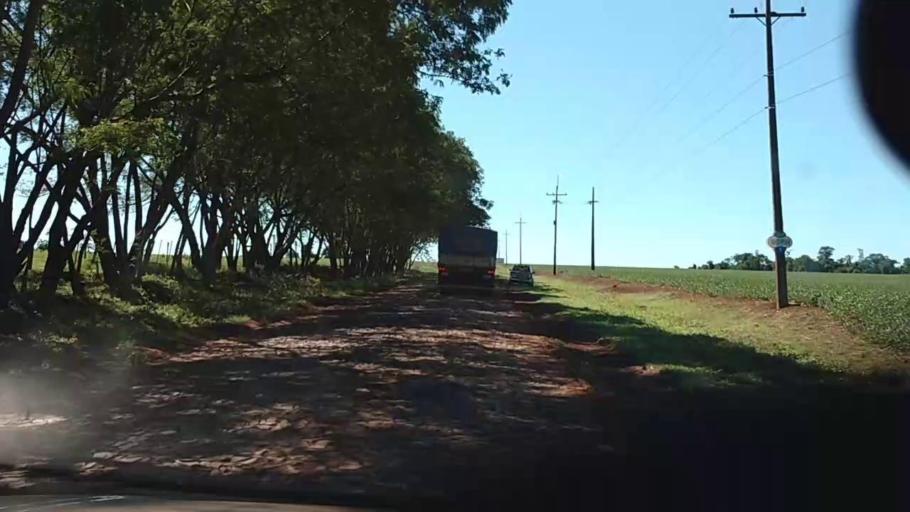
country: PY
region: Alto Parana
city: Naranjal
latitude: -25.9579
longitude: -55.1387
